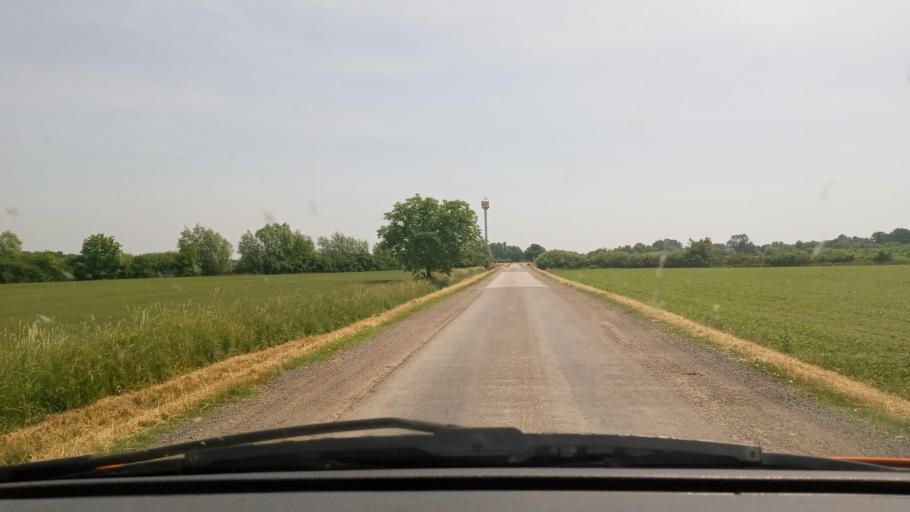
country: HU
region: Baranya
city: Szigetvar
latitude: 45.9807
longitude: 17.7396
